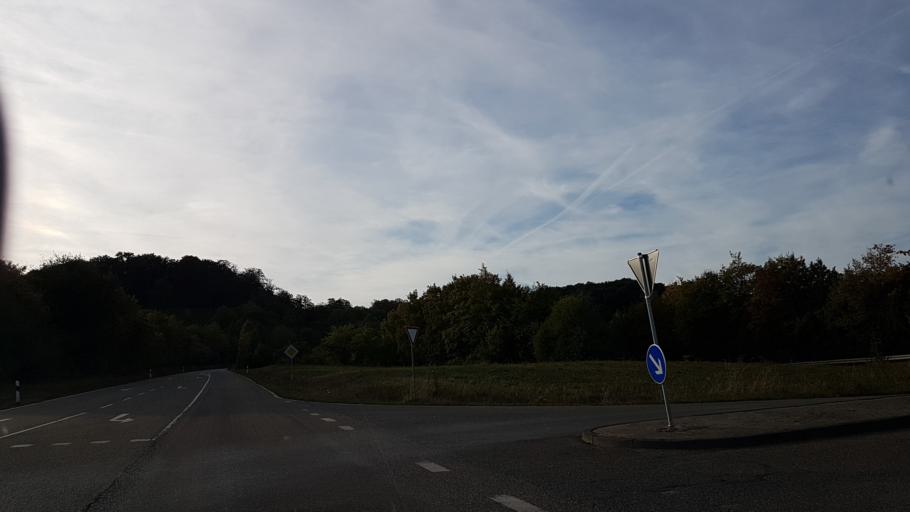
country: DE
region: Baden-Wuerttemberg
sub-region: Regierungsbezirk Stuttgart
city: Eberstadt
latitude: 49.1864
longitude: 9.3331
